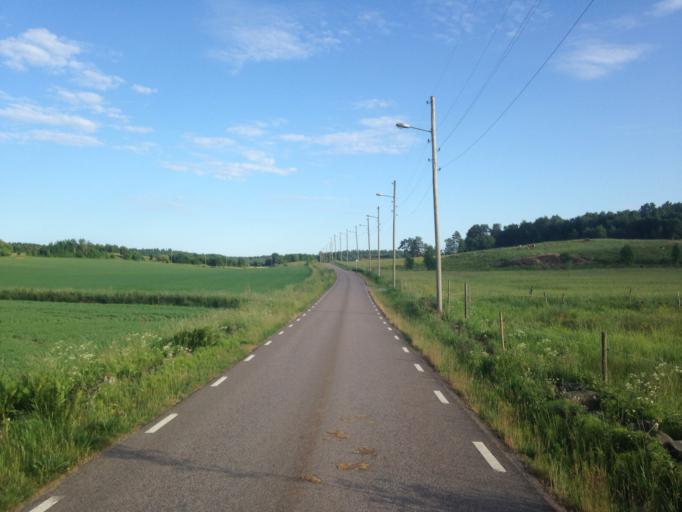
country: SE
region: Vaestra Goetaland
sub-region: Goteborg
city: Majorna
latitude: 57.7970
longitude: 11.8858
